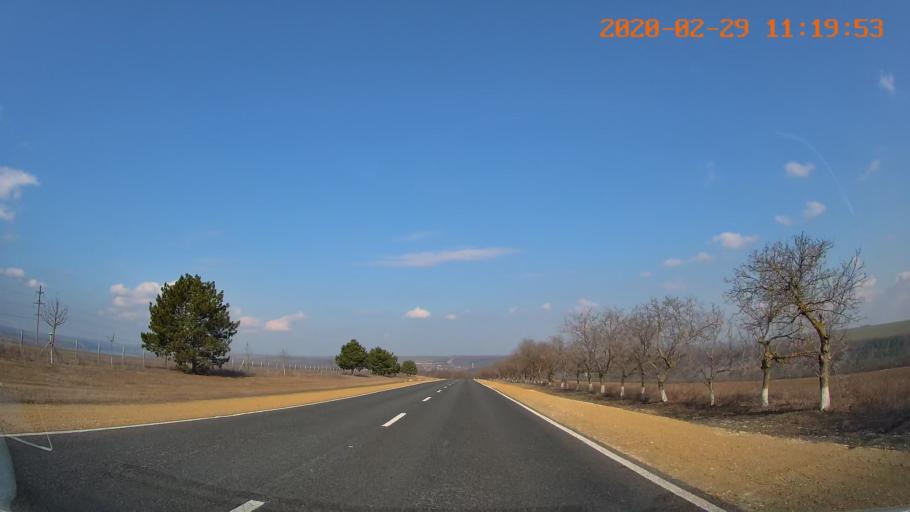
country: MD
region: Telenesti
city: Cocieri
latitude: 47.3568
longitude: 29.1731
